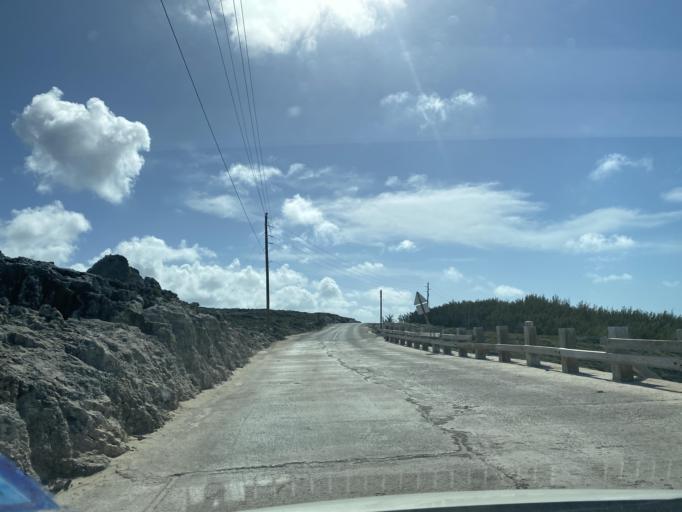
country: BS
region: Harbour Island
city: Dunmore Town
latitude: 25.4370
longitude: -76.6031
